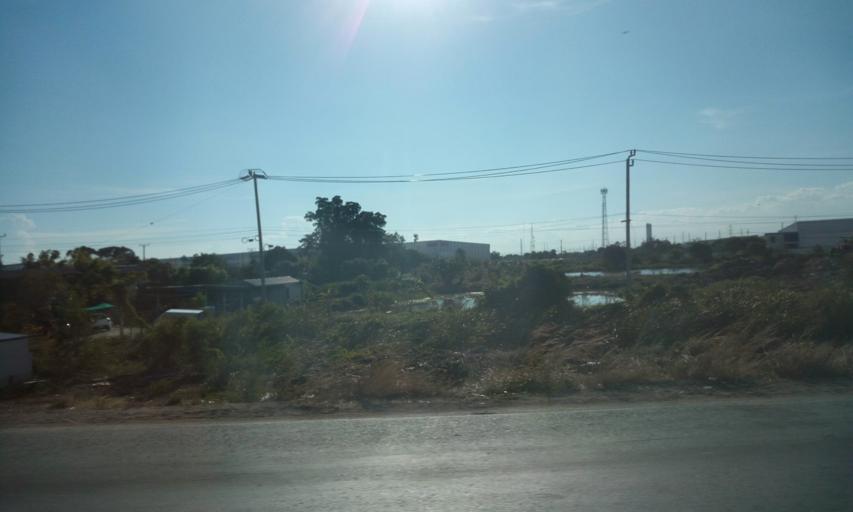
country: TH
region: Samut Prakan
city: Bang Bo District
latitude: 13.5774
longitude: 100.7575
